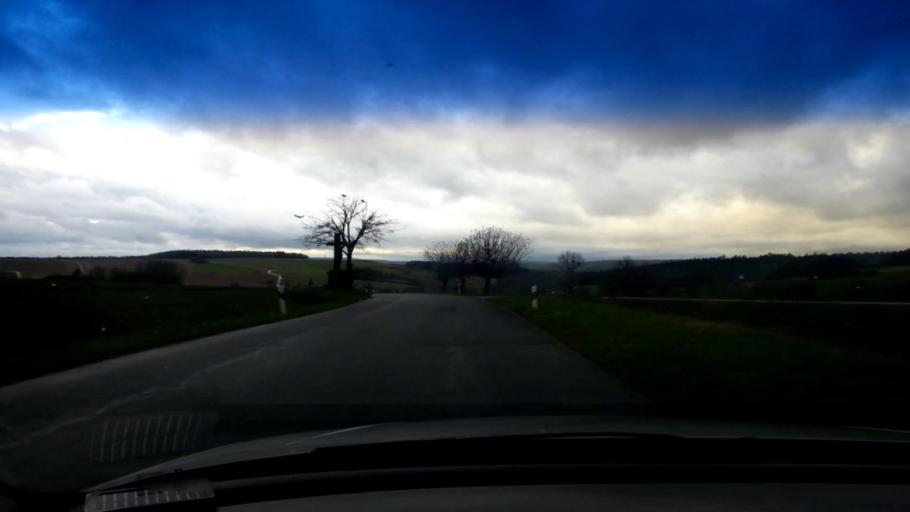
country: DE
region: Bavaria
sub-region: Upper Franconia
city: Ebensfeld
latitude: 50.0335
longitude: 10.9836
